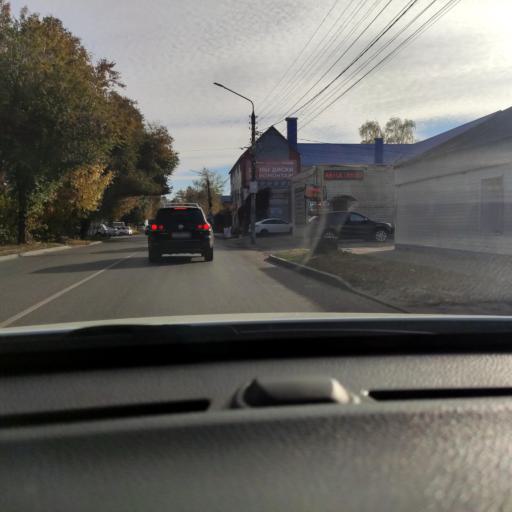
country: RU
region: Voronezj
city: Voronezh
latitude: 51.6826
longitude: 39.2065
